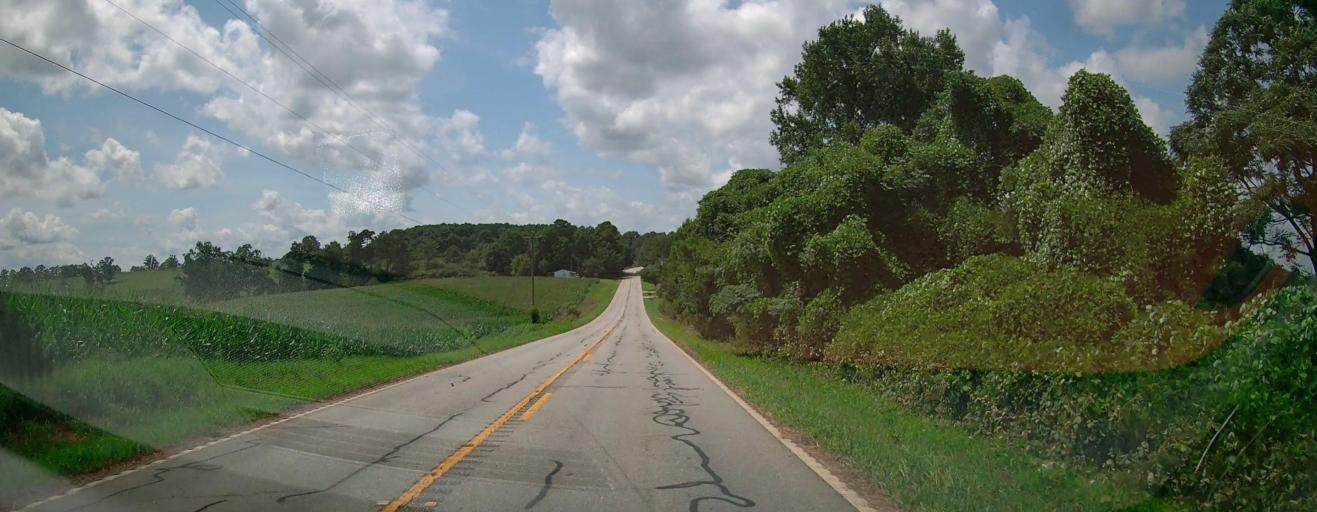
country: US
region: Georgia
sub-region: Carroll County
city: Bowdon
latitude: 33.4158
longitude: -85.2608
